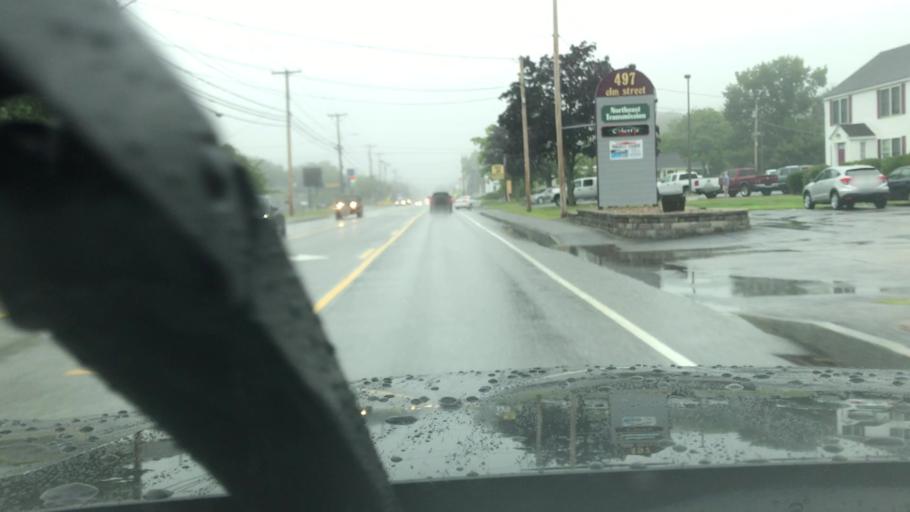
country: US
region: Maine
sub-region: York County
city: Biddeford
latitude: 43.4754
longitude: -70.4786
